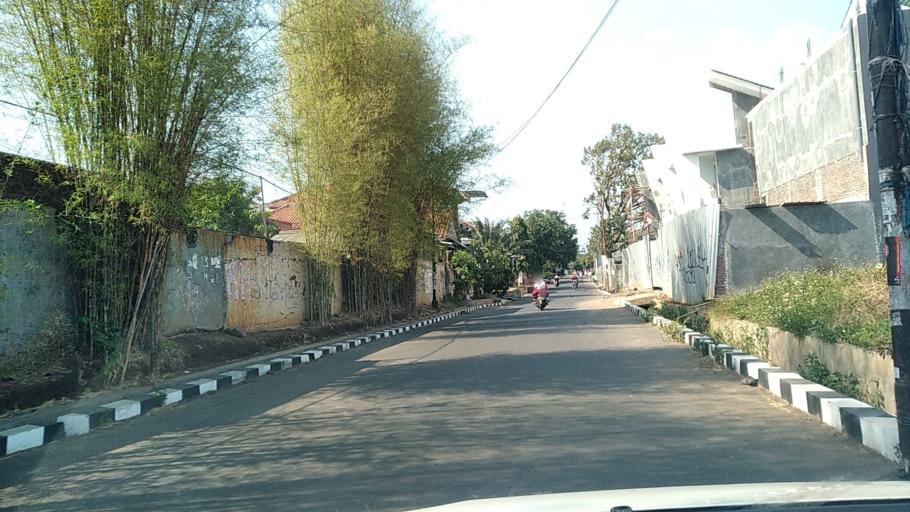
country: ID
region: Central Java
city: Semarang
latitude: -7.0654
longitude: 110.4191
